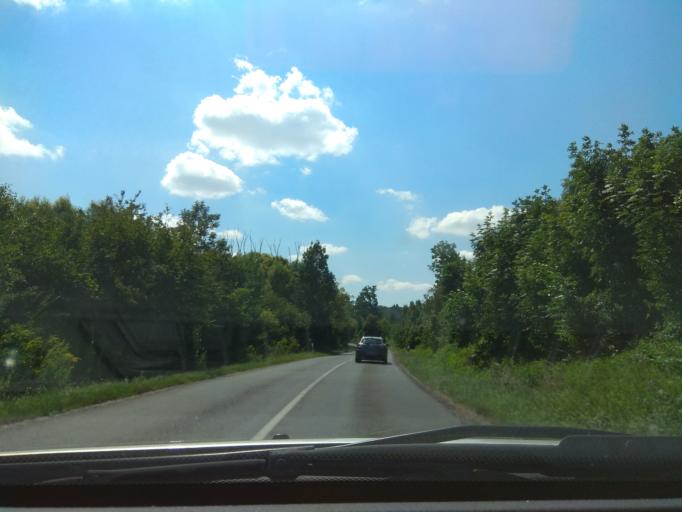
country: HU
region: Borsod-Abauj-Zemplen
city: Harsany
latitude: 48.0022
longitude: 20.7600
